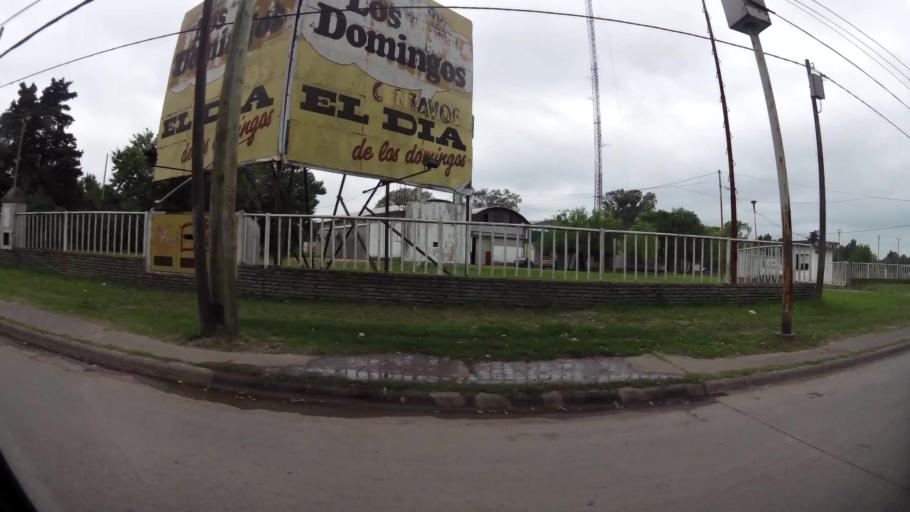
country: AR
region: Buenos Aires
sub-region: Partido de La Plata
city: La Plata
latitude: -34.9545
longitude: -58.0034
